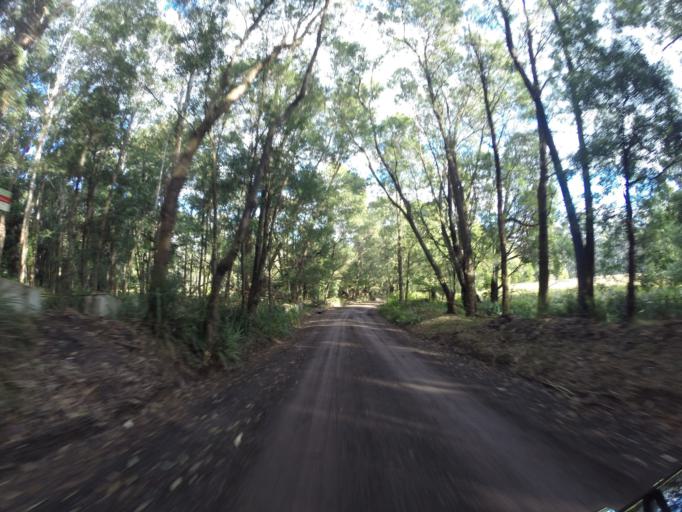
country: AU
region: New South Wales
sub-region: Wollongong
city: Cordeaux Heights
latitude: -34.4219
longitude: 150.7833
